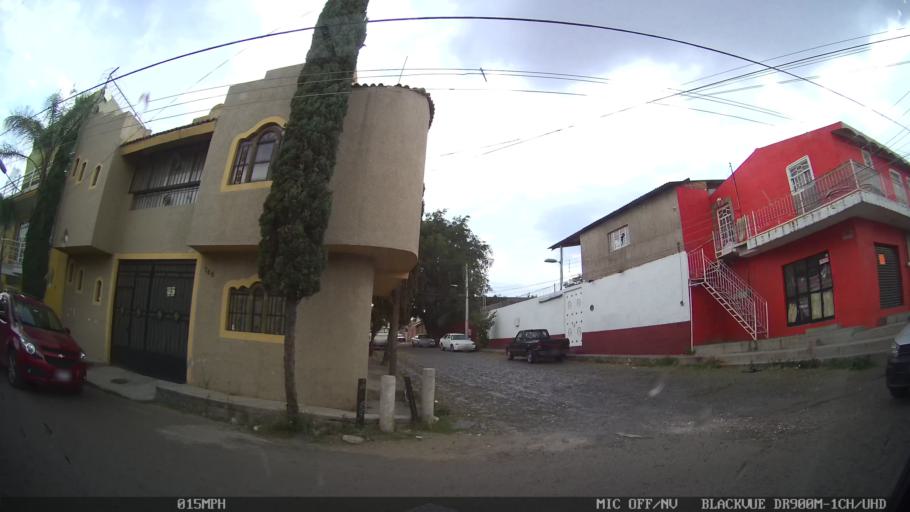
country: MX
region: Jalisco
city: Tonala
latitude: 20.6205
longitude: -103.2567
